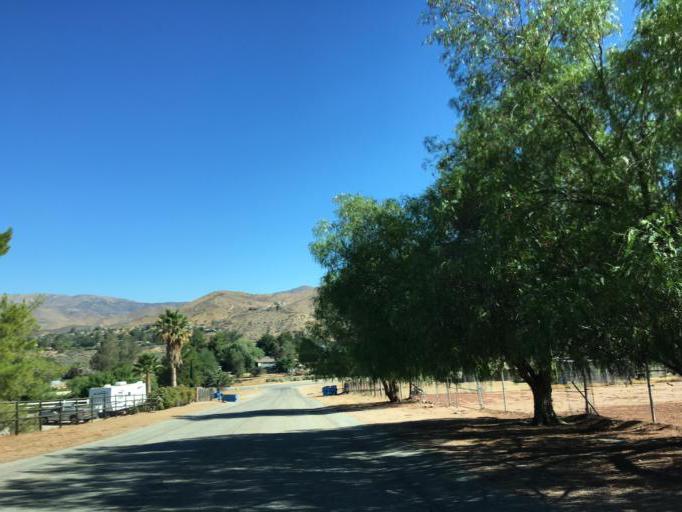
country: US
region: California
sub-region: Los Angeles County
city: Acton
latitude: 34.4629
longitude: -118.1764
